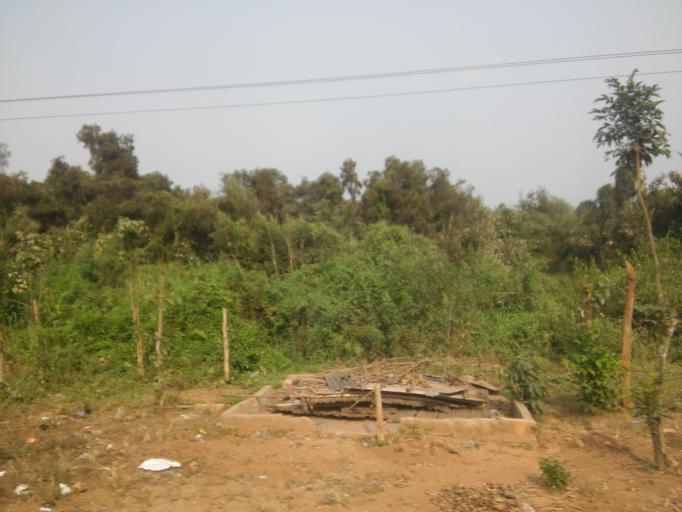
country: BJ
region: Queme
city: Porto-Novo
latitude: 6.4440
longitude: 2.6218
